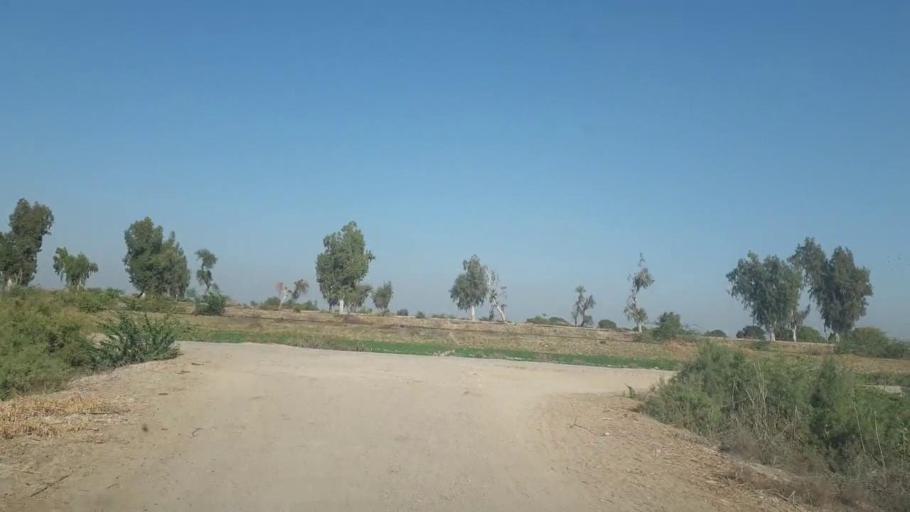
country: PK
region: Sindh
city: Mirpur Khas
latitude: 25.4541
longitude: 69.1434
